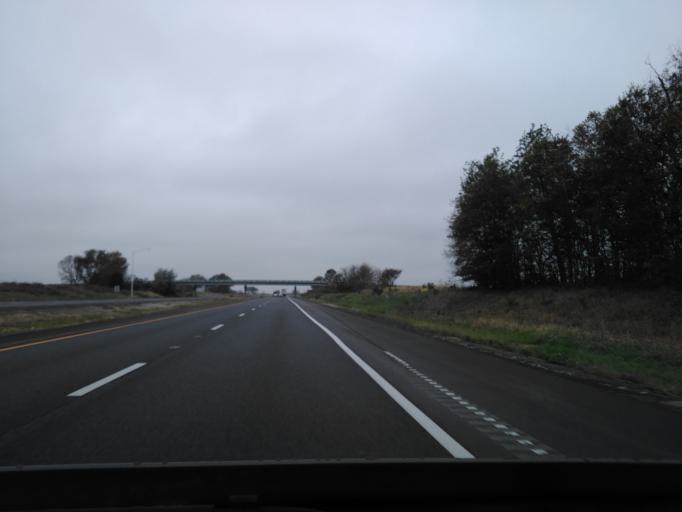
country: US
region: Illinois
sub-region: Madison County
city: Highland
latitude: 38.7863
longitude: -89.7050
